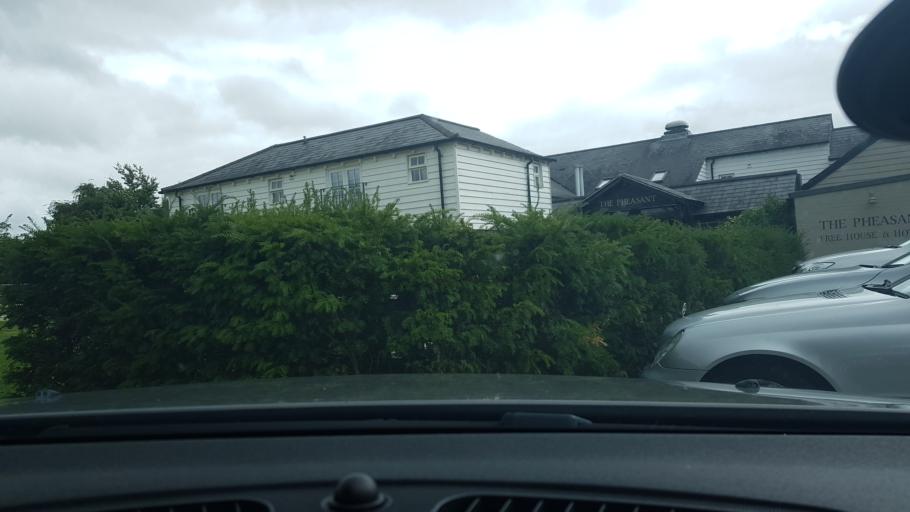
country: GB
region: England
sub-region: West Berkshire
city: Wickham
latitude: 51.4583
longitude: -1.4807
